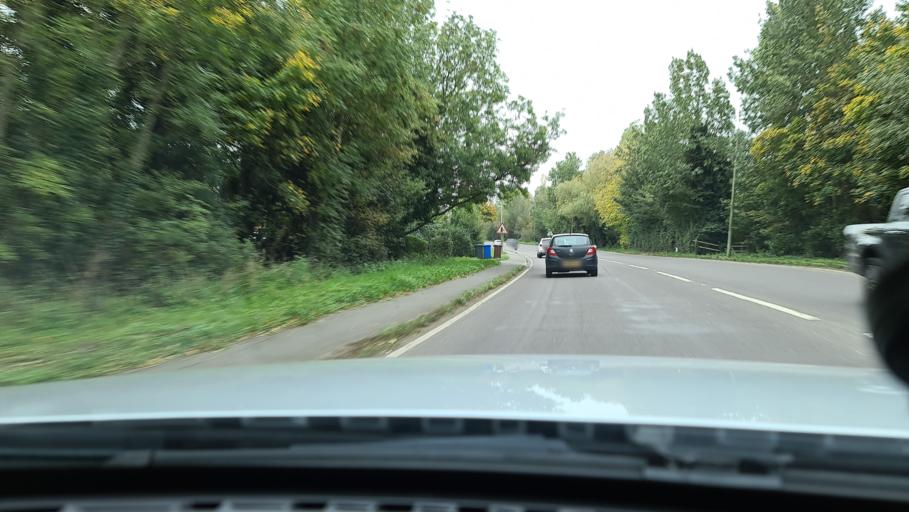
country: GB
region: England
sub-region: Oxfordshire
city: Bicester
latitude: 51.8815
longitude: -1.1330
